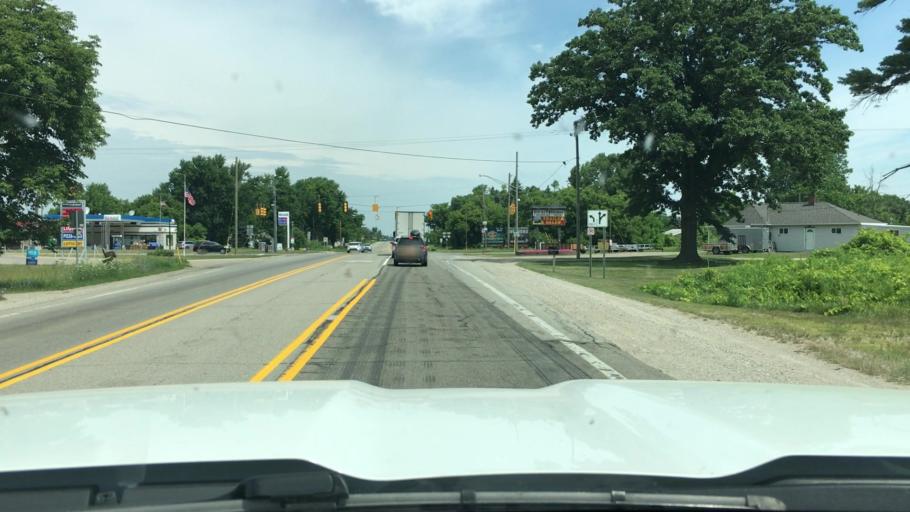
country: US
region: Michigan
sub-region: Sanilac County
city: Brown City
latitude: 43.2096
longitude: -83.0773
